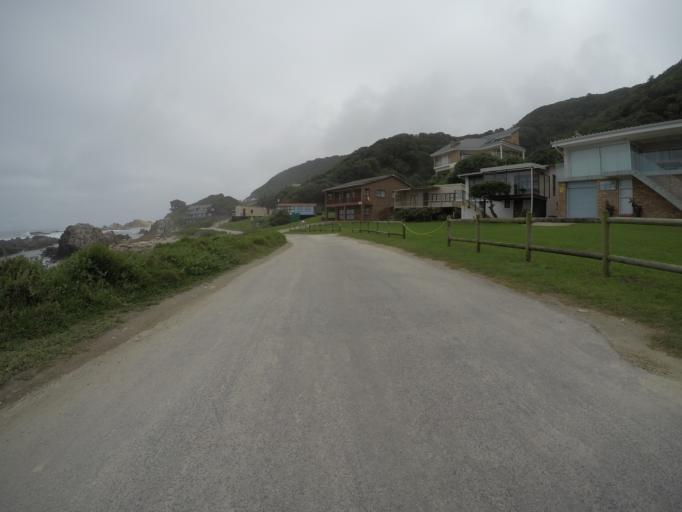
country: ZA
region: Eastern Cape
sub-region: Cacadu District Municipality
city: Kareedouw
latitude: -34.0726
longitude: 24.2251
